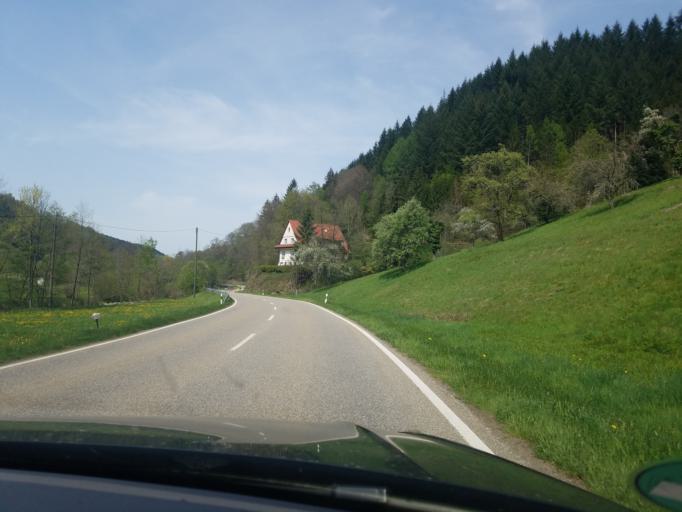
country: DE
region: Baden-Wuerttemberg
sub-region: Freiburg Region
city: Oppenau
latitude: 48.4422
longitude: 8.1711
